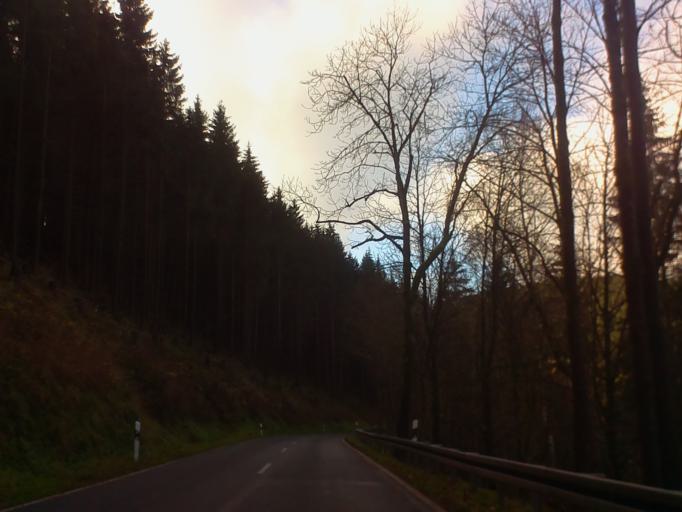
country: DE
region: Thuringia
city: Katzhutte
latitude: 50.5626
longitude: 11.0681
